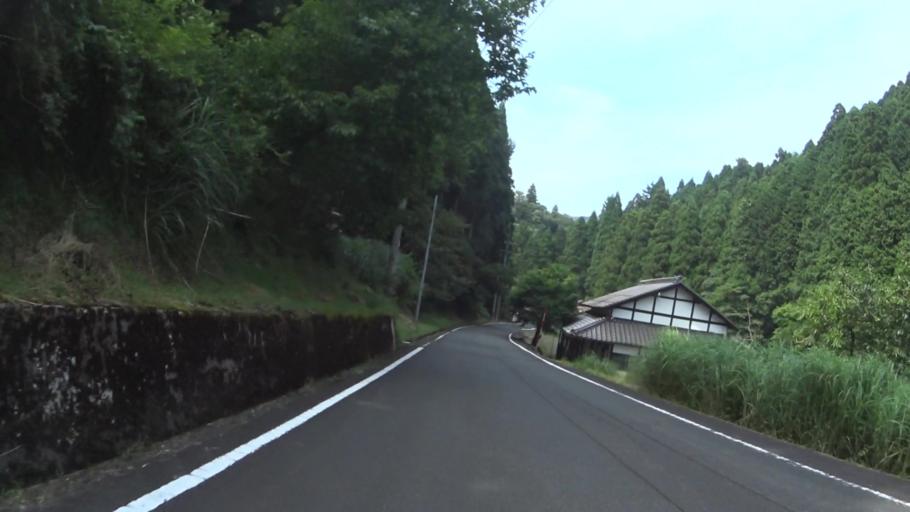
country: JP
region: Fukui
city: Obama
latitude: 35.3344
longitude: 135.6465
